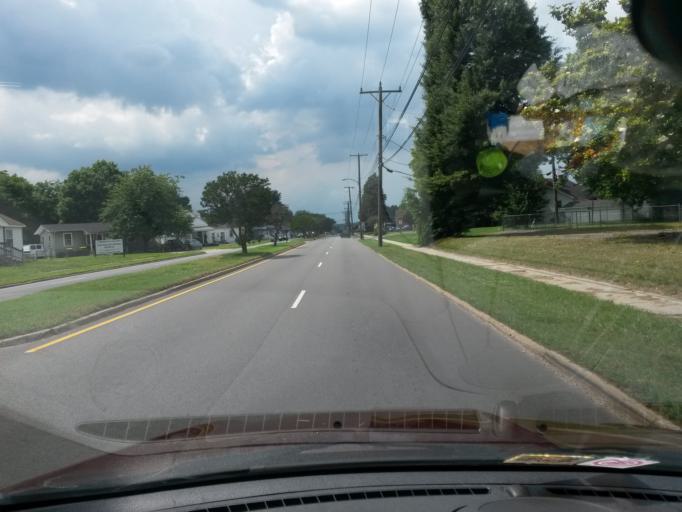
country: US
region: Virginia
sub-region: City of Hopewell
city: Hopewell
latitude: 37.3061
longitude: -77.2899
